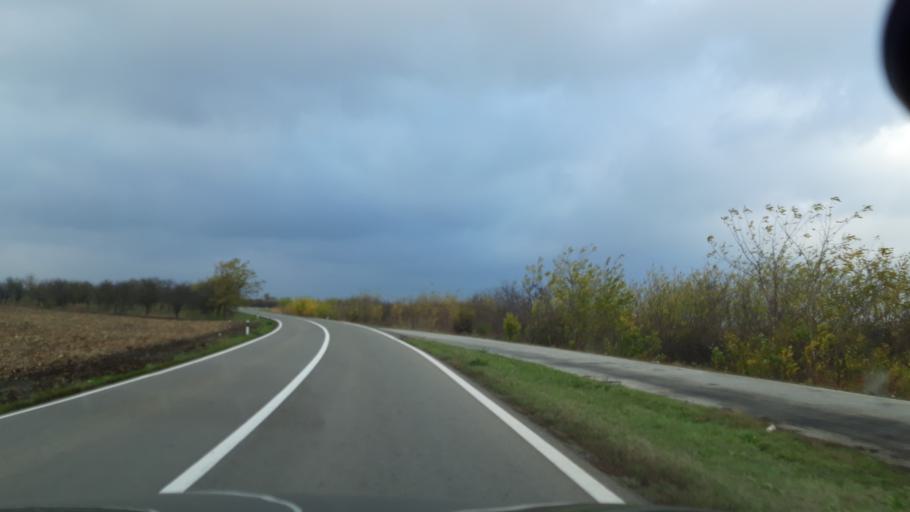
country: RS
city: Sanad
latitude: 45.9643
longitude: 20.1298
